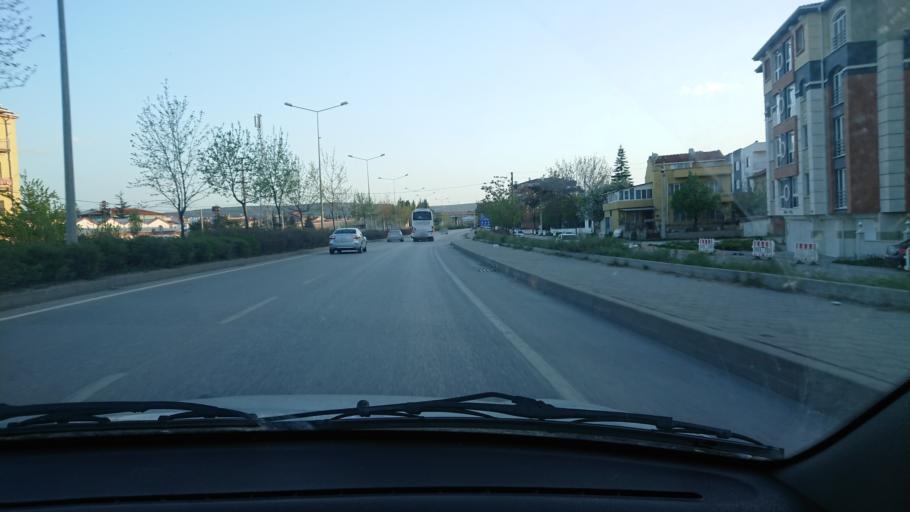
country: TR
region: Eskisehir
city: Eskisehir
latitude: 39.7716
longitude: 30.4830
